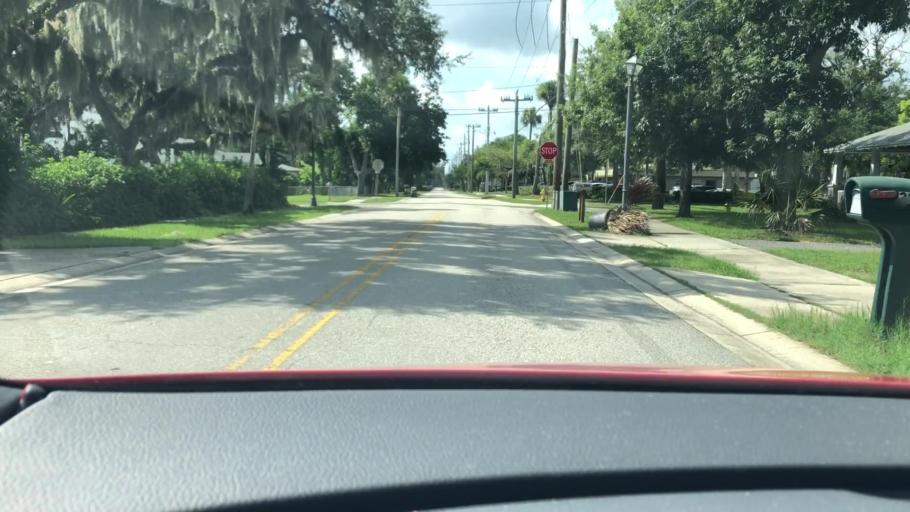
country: US
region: Florida
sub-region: Volusia County
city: Ormond Beach
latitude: 29.2768
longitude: -81.0551
